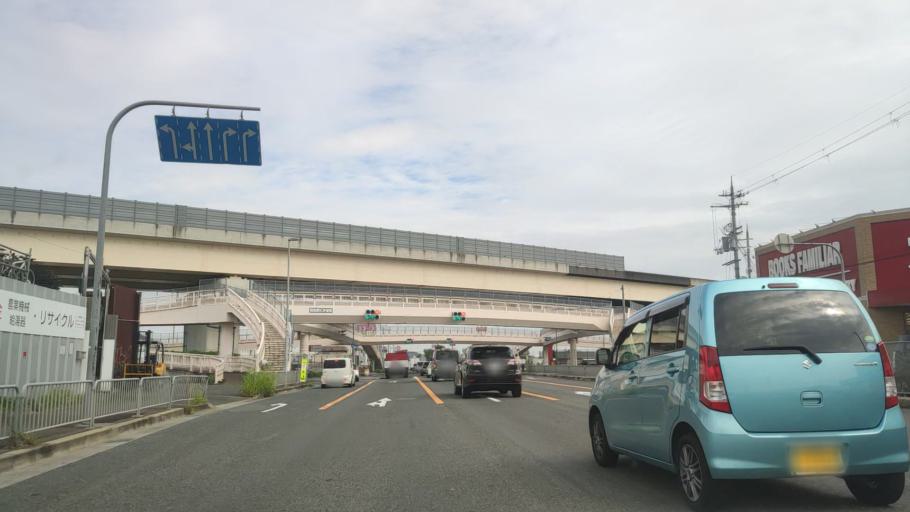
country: JP
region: Osaka
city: Tondabayashicho
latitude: 34.5330
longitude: 135.6048
